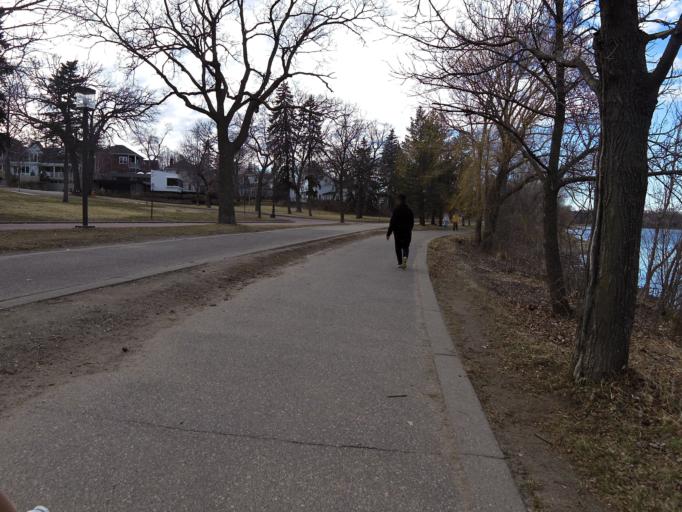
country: US
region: Minnesota
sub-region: Hennepin County
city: Saint Louis Park
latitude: 44.9344
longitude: -93.3122
